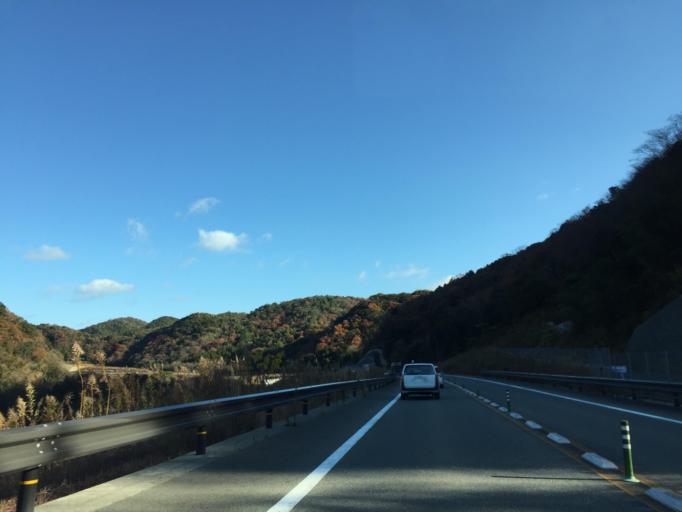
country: JP
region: Wakayama
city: Wakayama-shi
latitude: 34.3026
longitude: 135.1591
